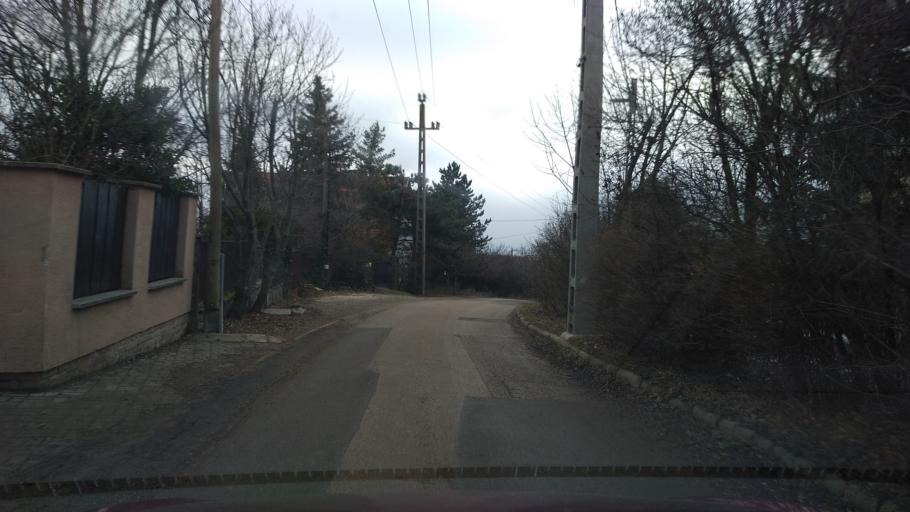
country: HU
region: Pest
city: Szentendre
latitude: 47.6990
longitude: 19.0517
